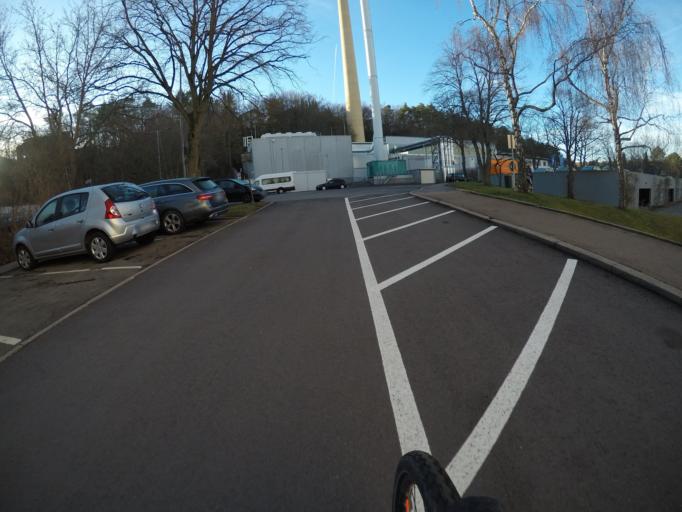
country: DE
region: Baden-Wuerttemberg
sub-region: Regierungsbezirk Stuttgart
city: Boeblingen
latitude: 48.6748
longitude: 9.0050
